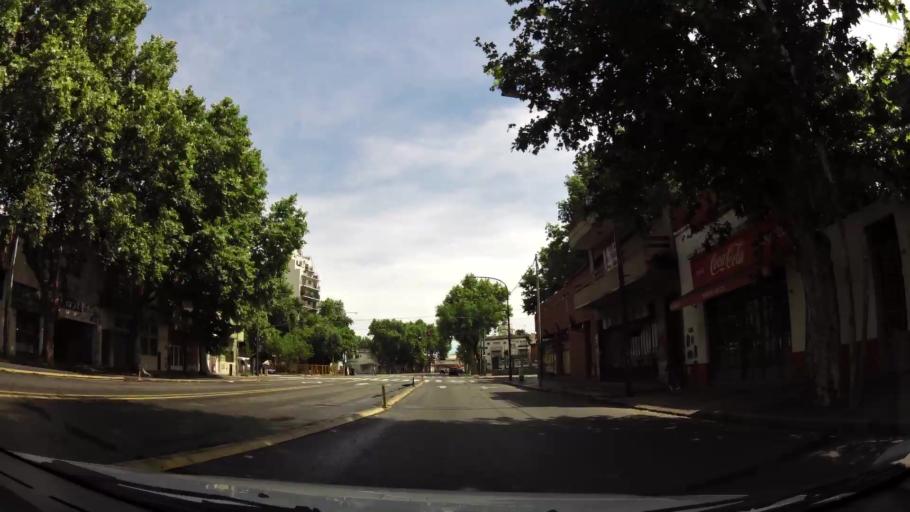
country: AR
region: Buenos Aires F.D.
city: Villa Santa Rita
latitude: -34.6093
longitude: -58.4651
